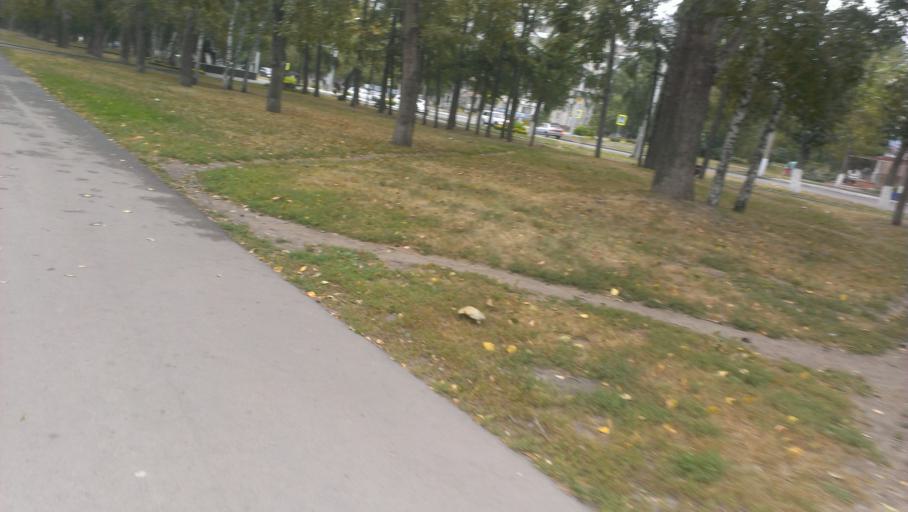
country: RU
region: Altai Krai
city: Novosilikatnyy
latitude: 53.3737
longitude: 83.6694
